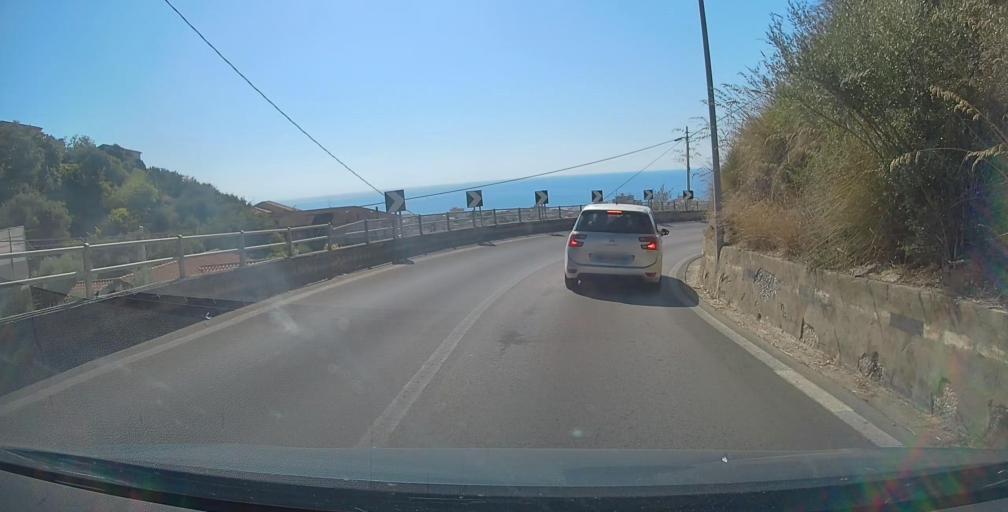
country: IT
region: Sicily
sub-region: Messina
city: Capo d'Orlando
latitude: 38.1571
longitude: 14.7499
